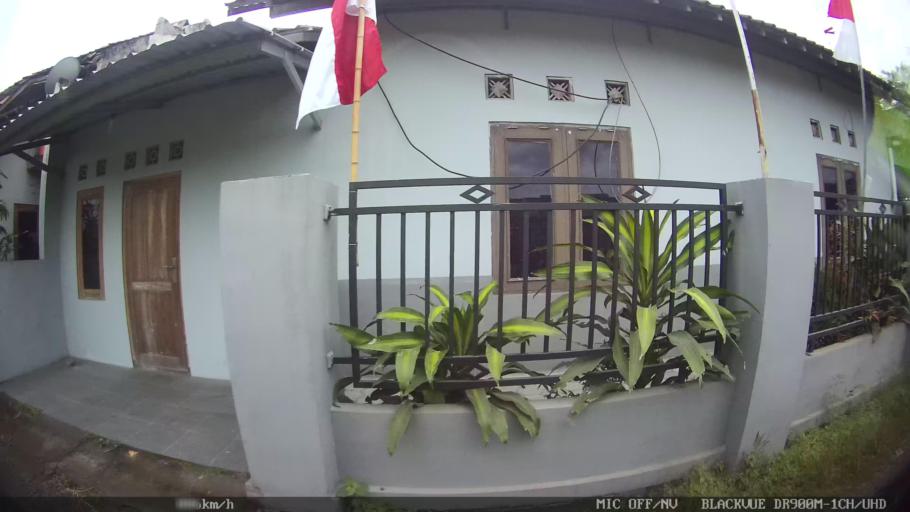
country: ID
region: Daerah Istimewa Yogyakarta
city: Sewon
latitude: -7.8334
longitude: 110.4108
